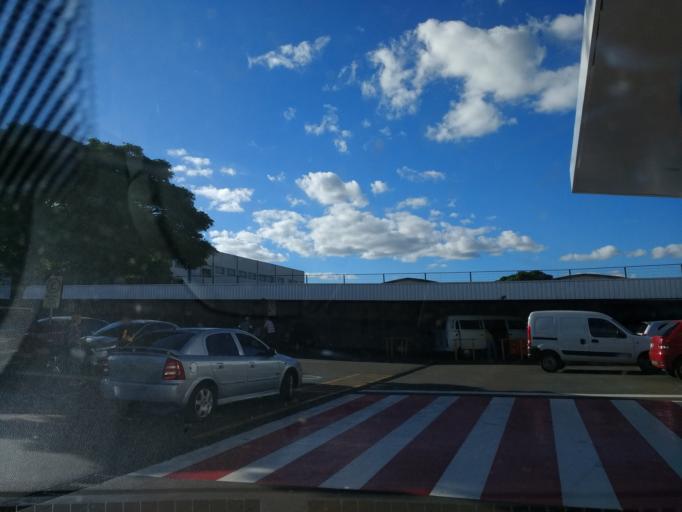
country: BR
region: Parana
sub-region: Londrina
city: Londrina
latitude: -23.3307
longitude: -51.1510
